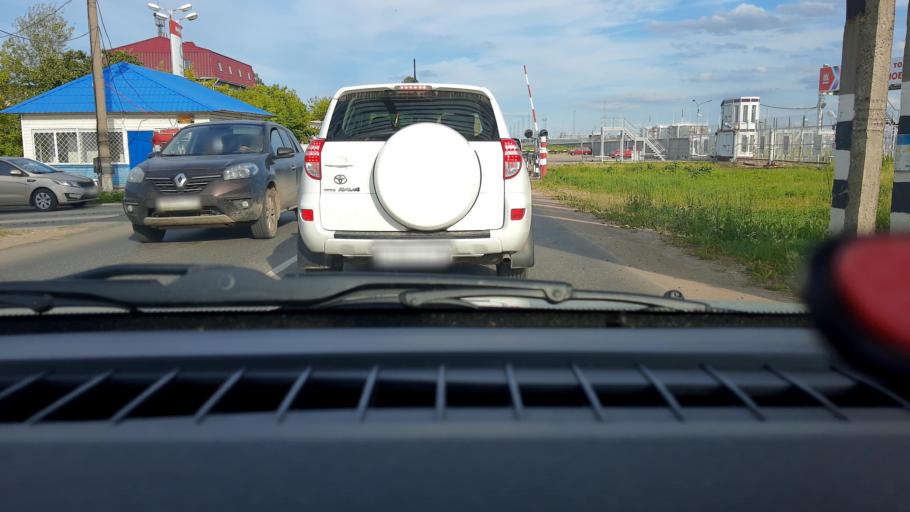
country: RU
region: Nizjnij Novgorod
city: Kstovo
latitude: 56.1247
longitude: 44.1258
